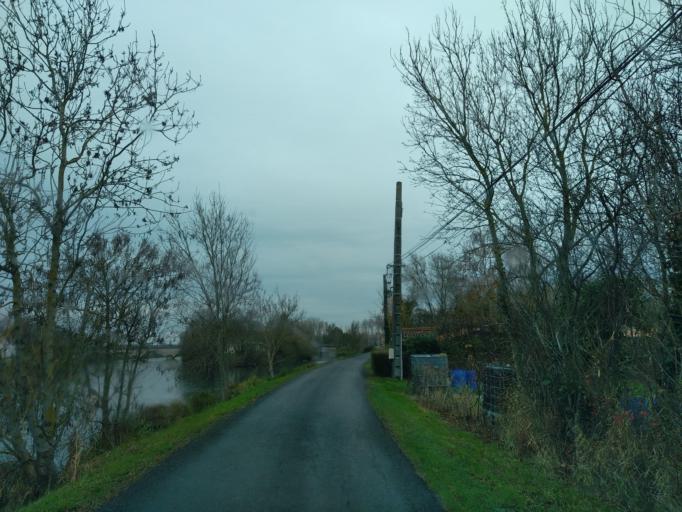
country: FR
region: Pays de la Loire
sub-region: Departement de la Vendee
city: Maillezais
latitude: 46.3197
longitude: -0.7854
